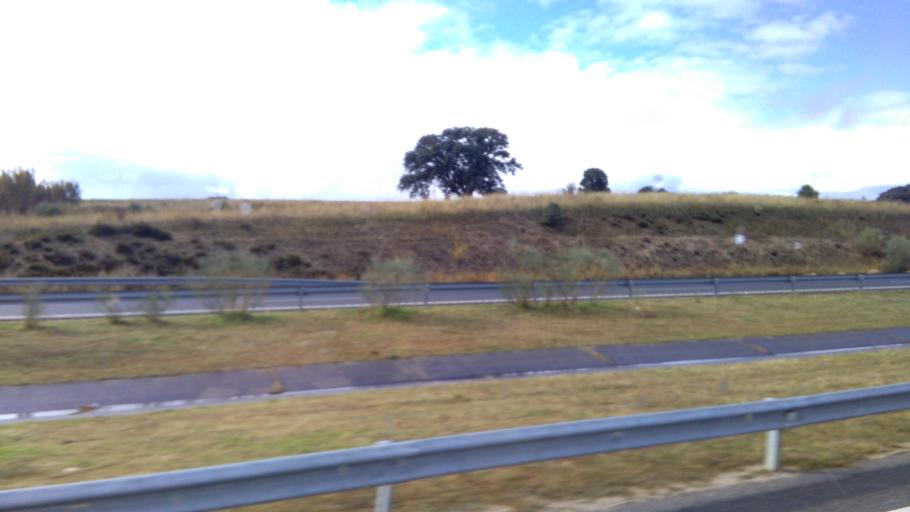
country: ES
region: Madrid
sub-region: Provincia de Madrid
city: El Alamo
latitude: 40.2620
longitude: -3.9937
